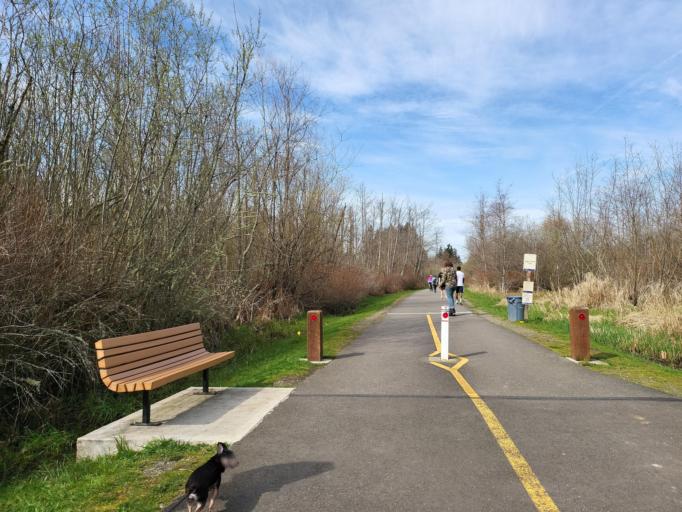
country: US
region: Washington
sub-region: King County
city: East Hill-Meridian
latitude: 47.4087
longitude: -122.1593
